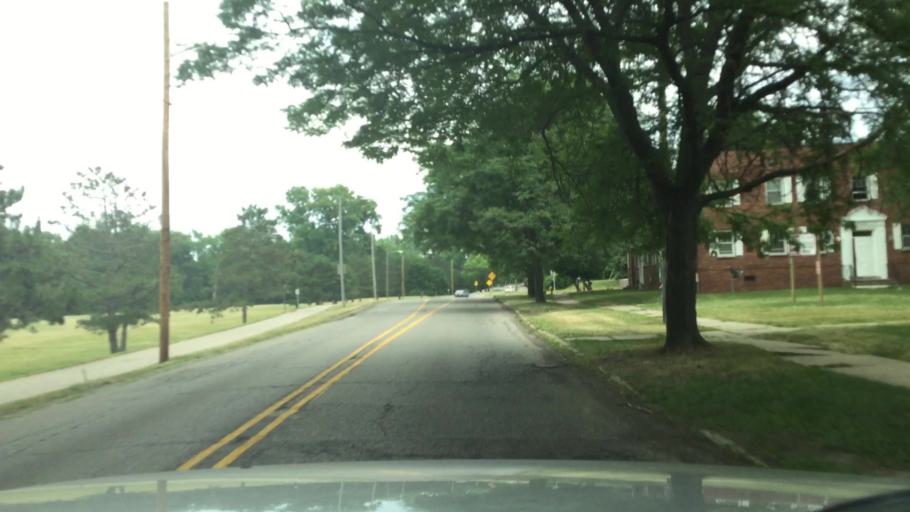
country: US
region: Michigan
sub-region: Genesee County
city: Flint
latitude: 43.0125
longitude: -83.7243
